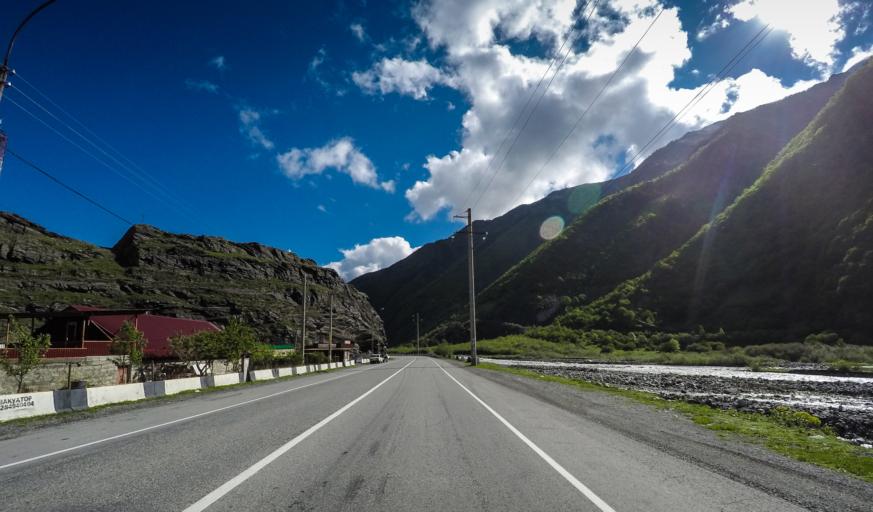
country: RU
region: Ingushetiya
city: Dzhayrakh
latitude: 42.7964
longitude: 44.6368
